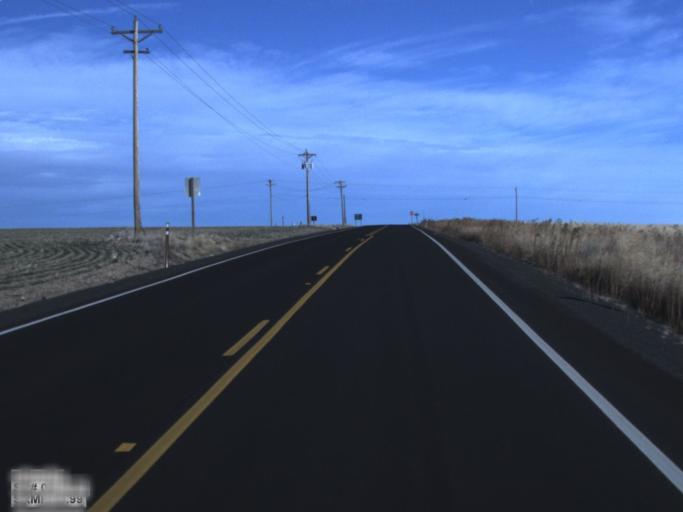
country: US
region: Washington
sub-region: Adams County
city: Ritzville
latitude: 47.1284
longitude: -118.6651
